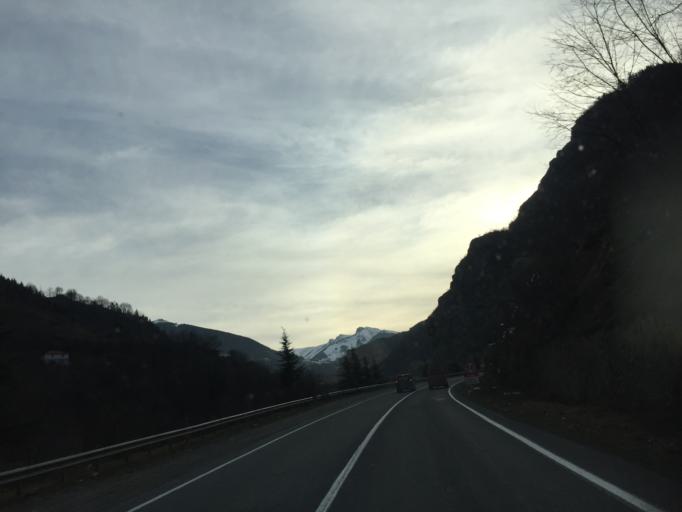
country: TR
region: Trabzon
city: Macka
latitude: 40.7281
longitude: 39.5271
